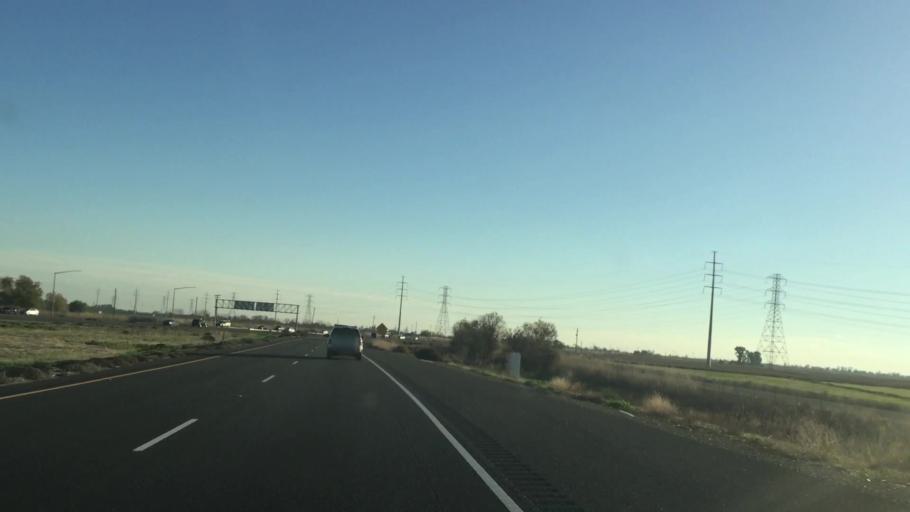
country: US
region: California
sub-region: Sacramento County
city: Elverta
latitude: 38.8474
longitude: -121.5450
